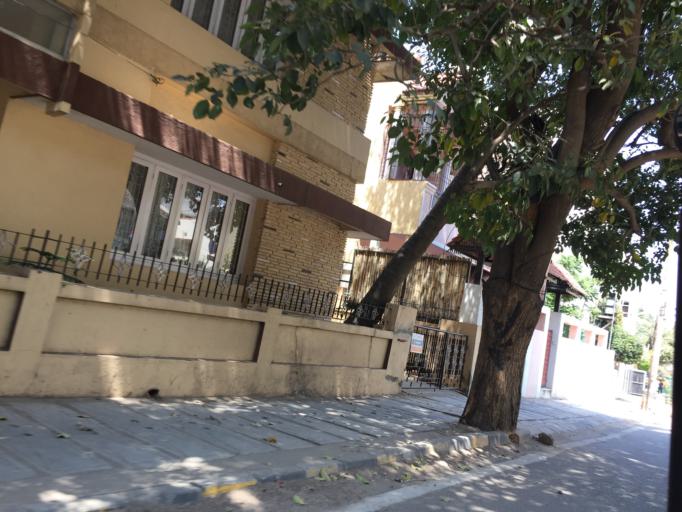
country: IN
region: Karnataka
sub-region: Bangalore Urban
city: Bangalore
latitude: 13.0041
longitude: 77.6247
